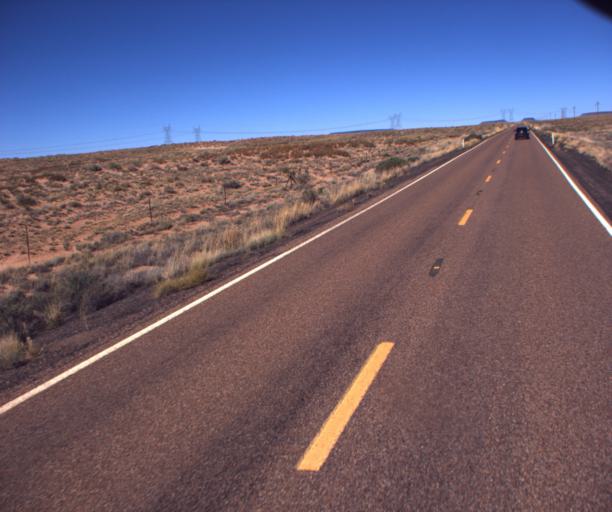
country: US
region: Arizona
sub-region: Navajo County
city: Holbrook
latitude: 35.1488
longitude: -110.0868
